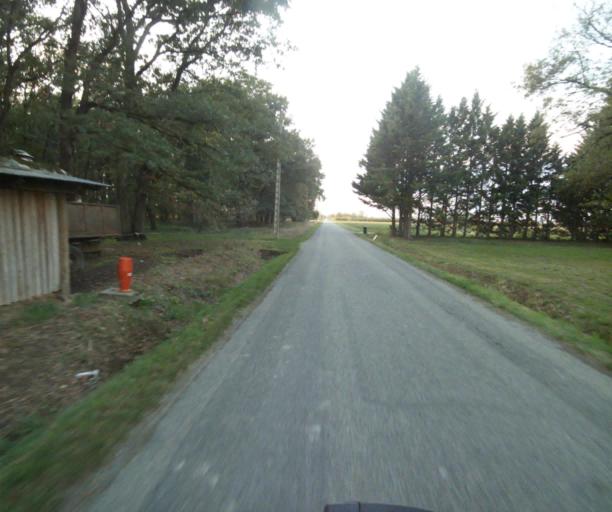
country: FR
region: Midi-Pyrenees
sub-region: Departement du Tarn-et-Garonne
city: Verdun-sur-Garonne
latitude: 43.8292
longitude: 1.2295
